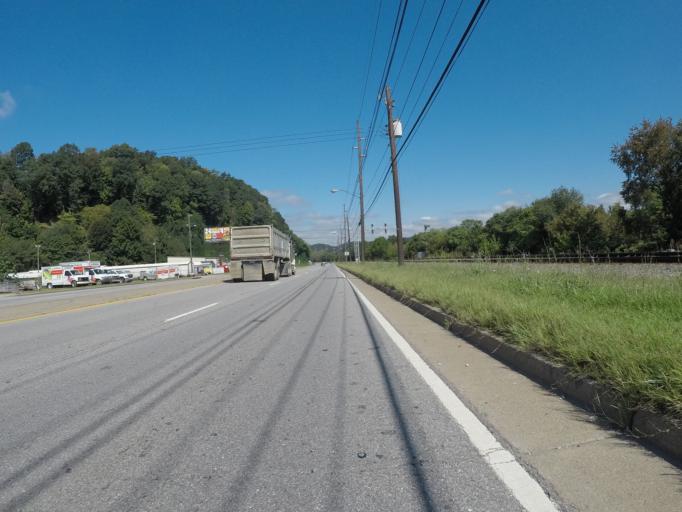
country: US
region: Kentucky
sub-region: Boyd County
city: Ashland
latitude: 38.4556
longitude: -82.6126
